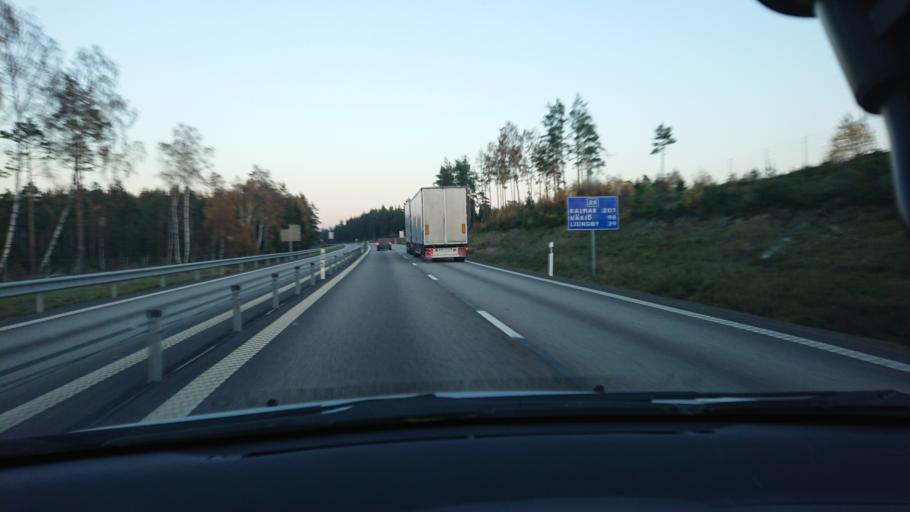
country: SE
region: Halland
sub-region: Laholms Kommun
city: Knared
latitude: 56.7248
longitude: 13.3737
